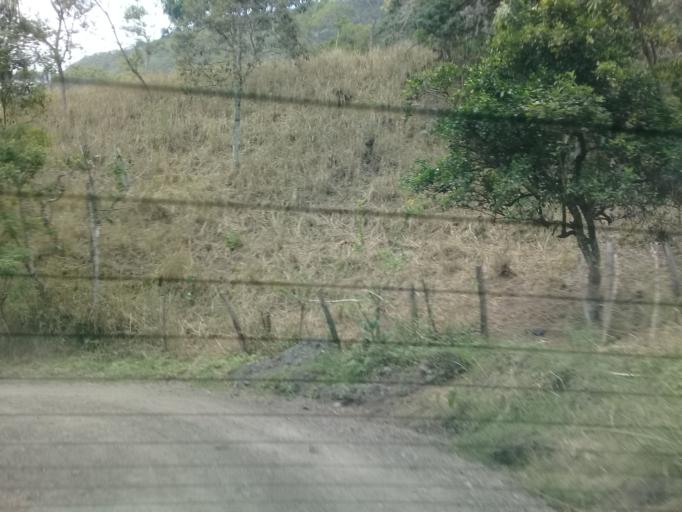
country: CO
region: Cundinamarca
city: Viani
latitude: 4.8680
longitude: -74.5390
